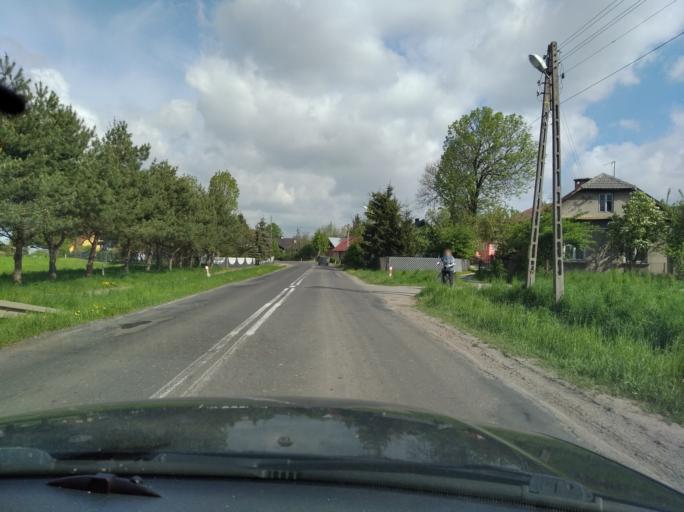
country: PL
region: Subcarpathian Voivodeship
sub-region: Powiat przeworski
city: Urzejowice
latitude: 50.0136
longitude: 22.4638
